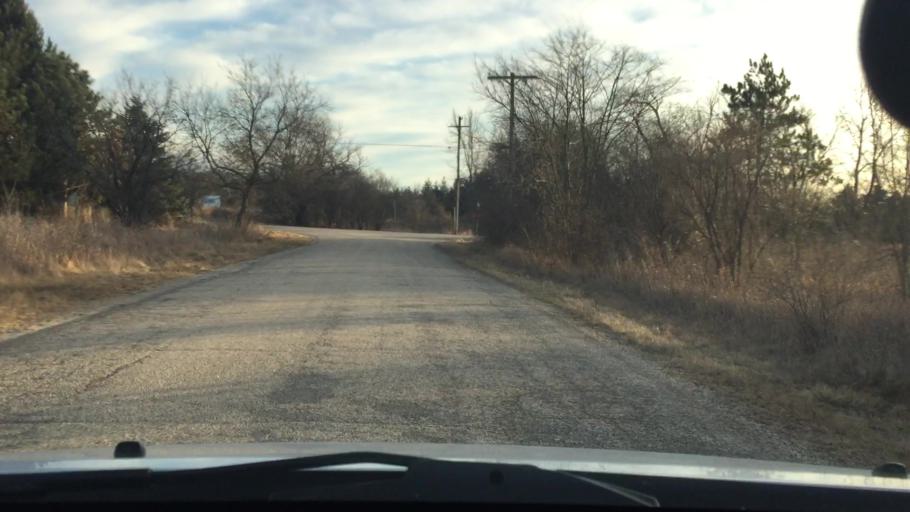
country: US
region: Wisconsin
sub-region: Waukesha County
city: North Prairie
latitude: 42.9309
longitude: -88.4345
